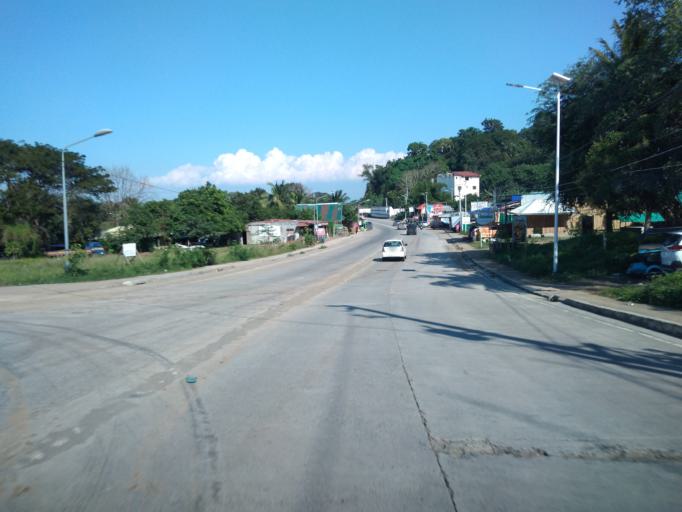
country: PH
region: Calabarzon
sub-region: Province of Laguna
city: Calamba
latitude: 14.1855
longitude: 121.1633
